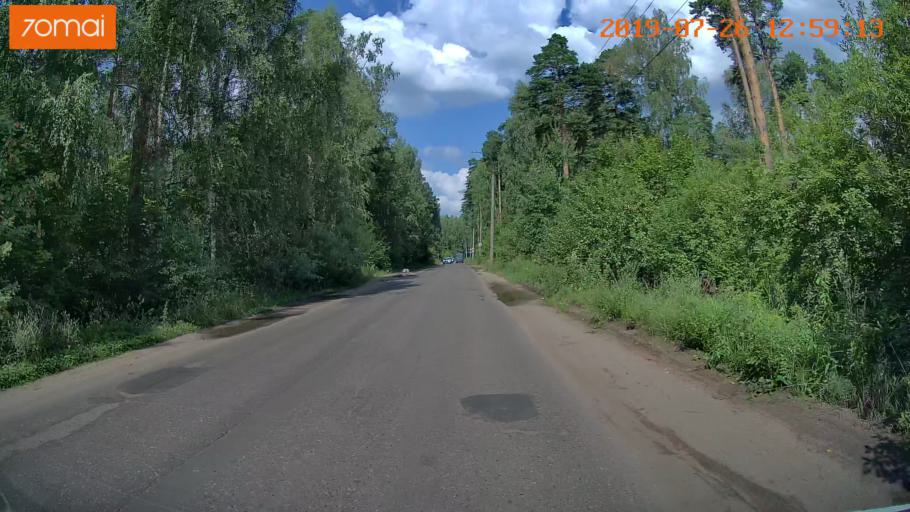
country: RU
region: Ivanovo
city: Bogorodskoye
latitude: 57.0275
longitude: 41.0208
